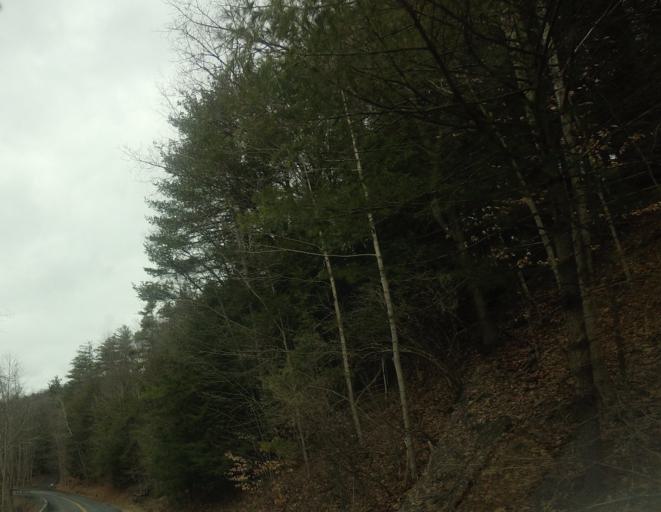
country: US
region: New York
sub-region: Tompkins County
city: Northwest Ithaca
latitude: 42.4371
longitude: -76.5486
